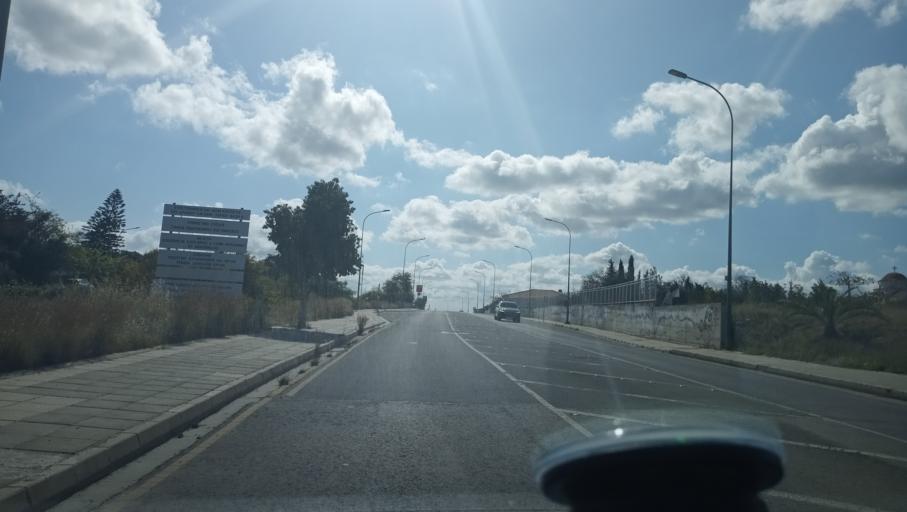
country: CY
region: Lefkosia
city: Geri
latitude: 35.1062
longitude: 33.4084
